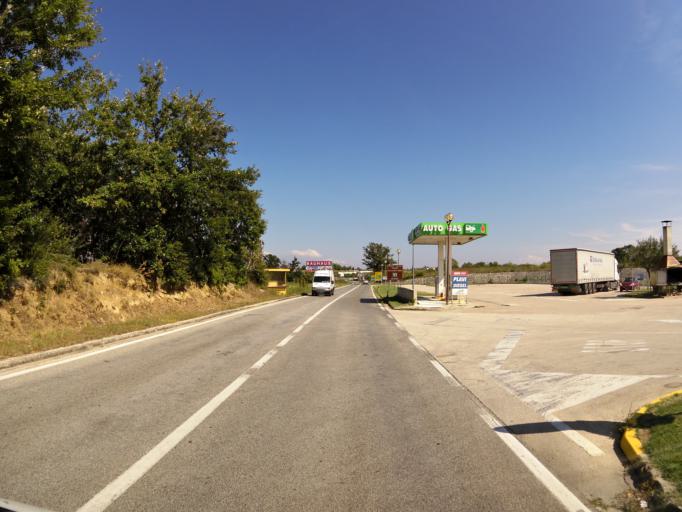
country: HR
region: Zadarska
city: Policnik
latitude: 44.1918
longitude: 15.4207
